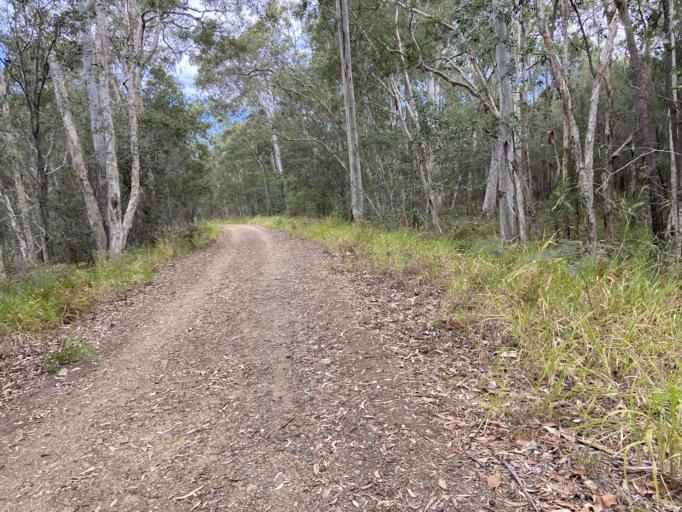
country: AU
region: Queensland
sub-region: Moreton Bay
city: Caboolture
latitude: -26.9544
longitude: 152.9557
